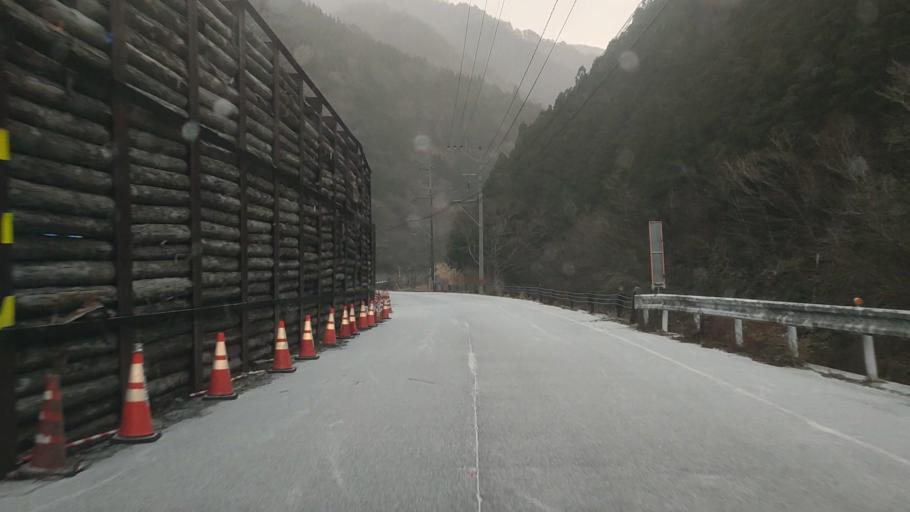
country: JP
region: Kumamoto
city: Matsubase
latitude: 32.5540
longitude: 130.9310
